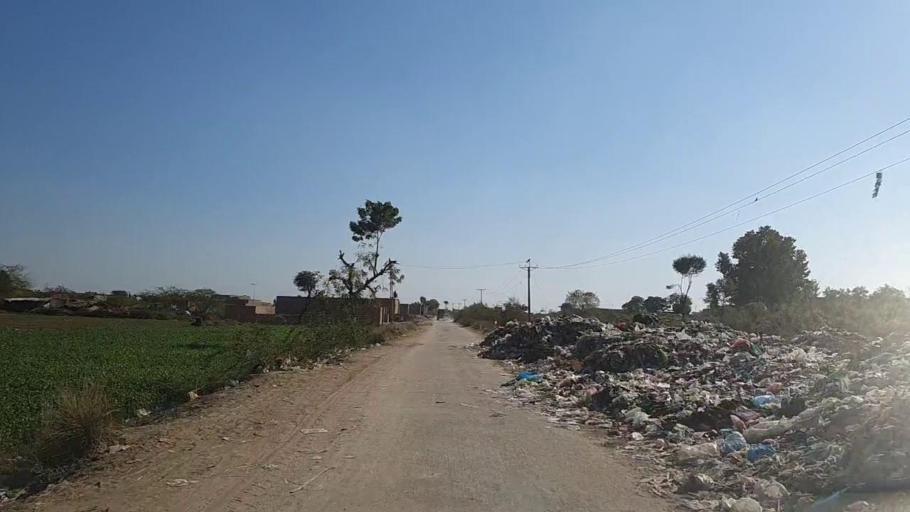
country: PK
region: Sindh
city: Nawabshah
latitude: 26.2424
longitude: 68.4232
